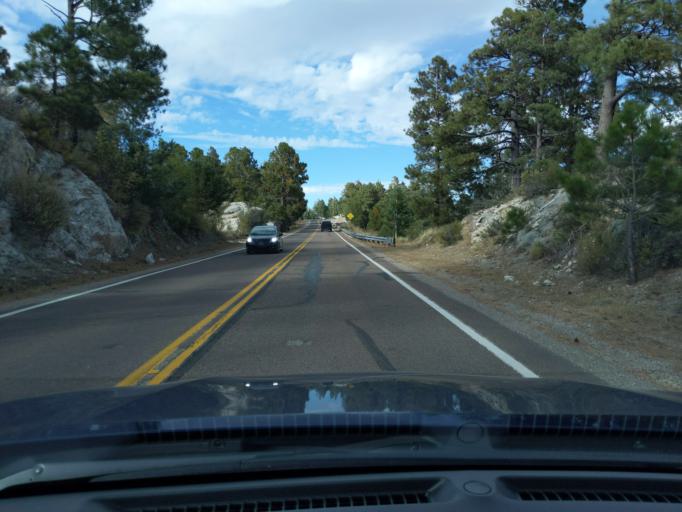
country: US
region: Arizona
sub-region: Pinal County
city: Oracle
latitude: 32.4370
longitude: -110.7523
